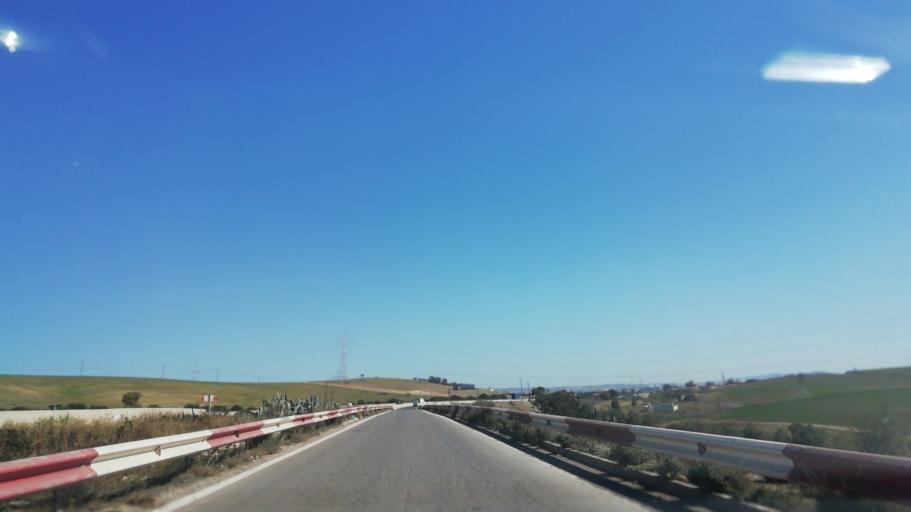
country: DZ
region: Oran
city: Sidi ech Chahmi
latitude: 35.5732
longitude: -0.5559
